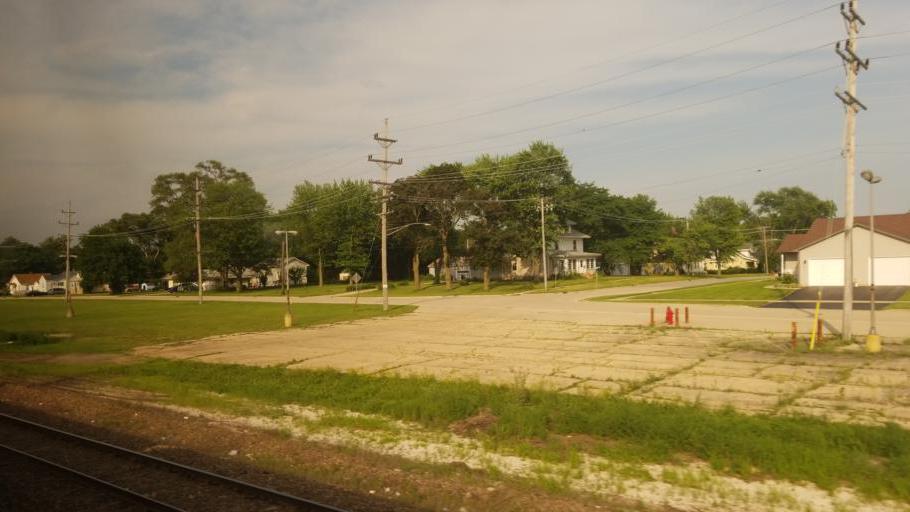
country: US
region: Illinois
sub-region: Kane County
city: Montgomery
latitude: 41.7263
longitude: -88.3477
